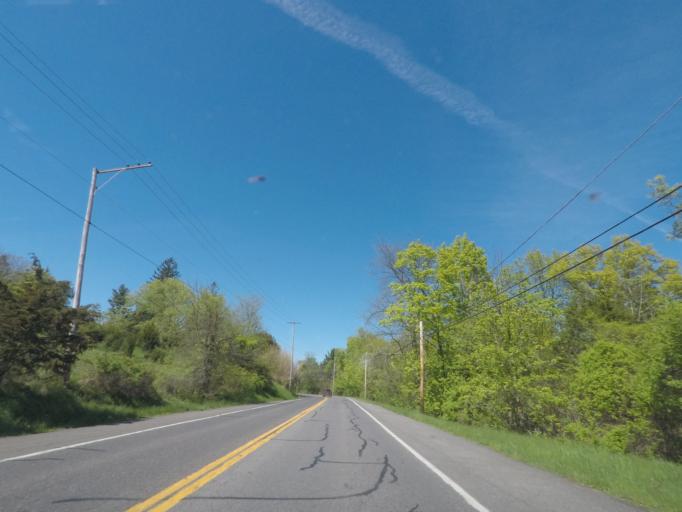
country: US
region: New York
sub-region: Ulster County
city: Saugerties
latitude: 42.1106
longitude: -73.9364
